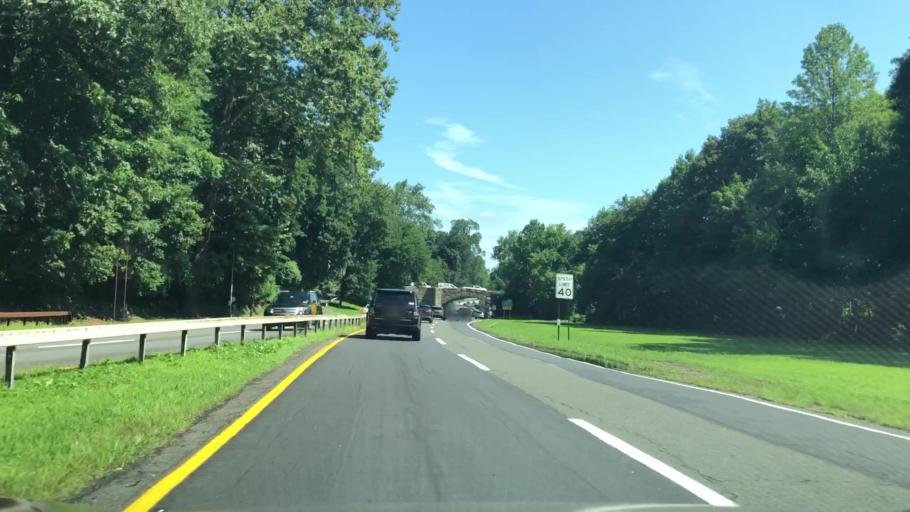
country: US
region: New York
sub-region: Westchester County
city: Greenville
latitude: 40.9871
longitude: -73.8116
